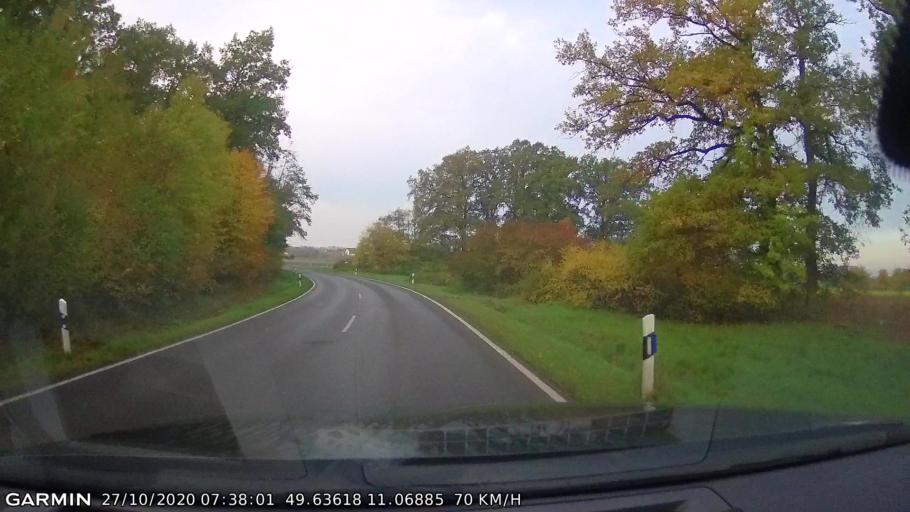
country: DE
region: Bavaria
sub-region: Upper Franconia
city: Langensendelbach
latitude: 49.6360
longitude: 11.0688
